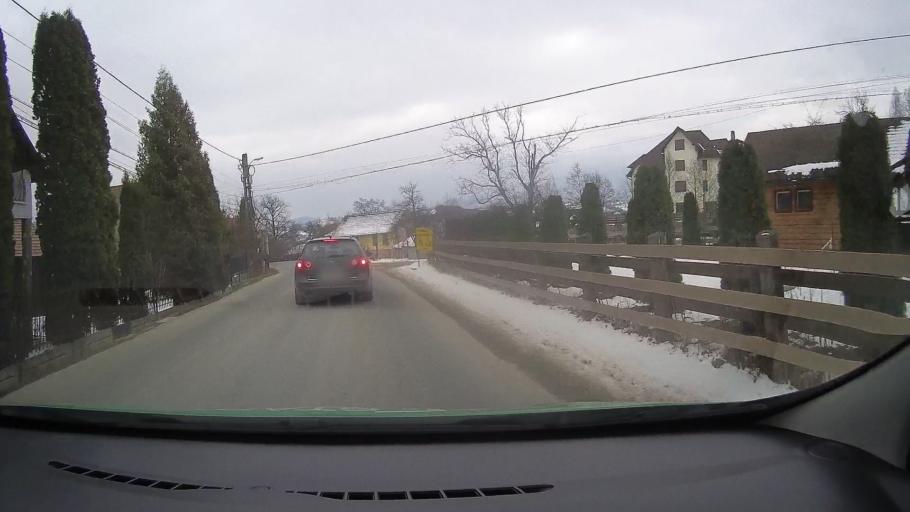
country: RO
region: Brasov
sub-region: Comuna Bran
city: Bran
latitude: 45.5290
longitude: 25.3584
